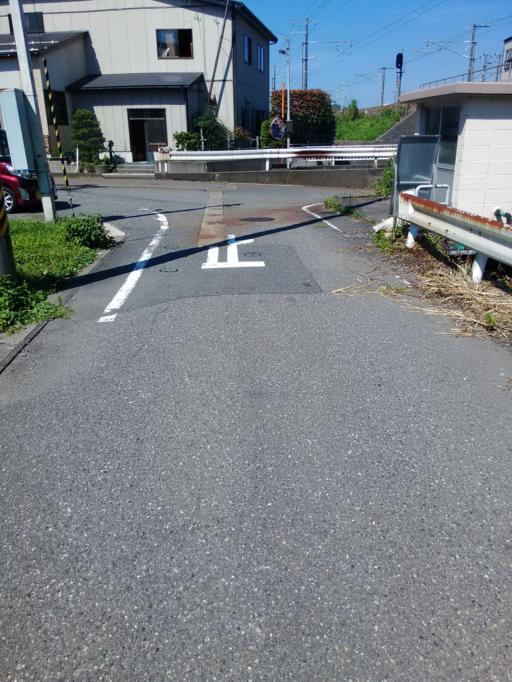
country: JP
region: Niigata
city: Itoigawa
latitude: 37.0503
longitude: 137.8864
